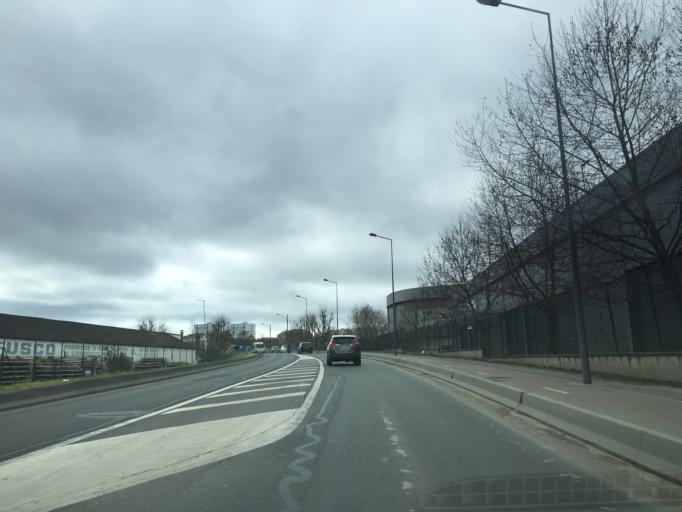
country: FR
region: Ile-de-France
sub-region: Departement du Val-de-Marne
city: Bonneuil-sur-Marne
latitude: 48.7785
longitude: 2.4915
